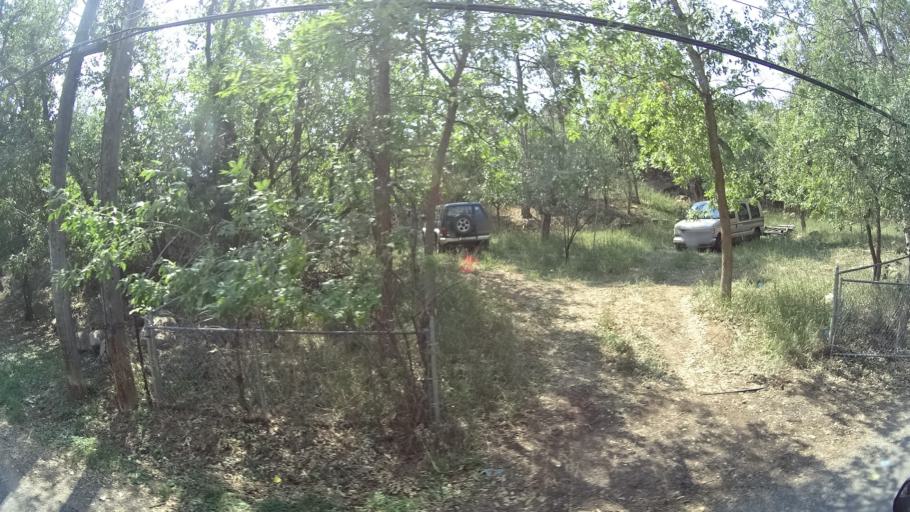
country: US
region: Colorado
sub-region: El Paso County
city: Colorado Springs
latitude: 38.7906
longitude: -104.8568
